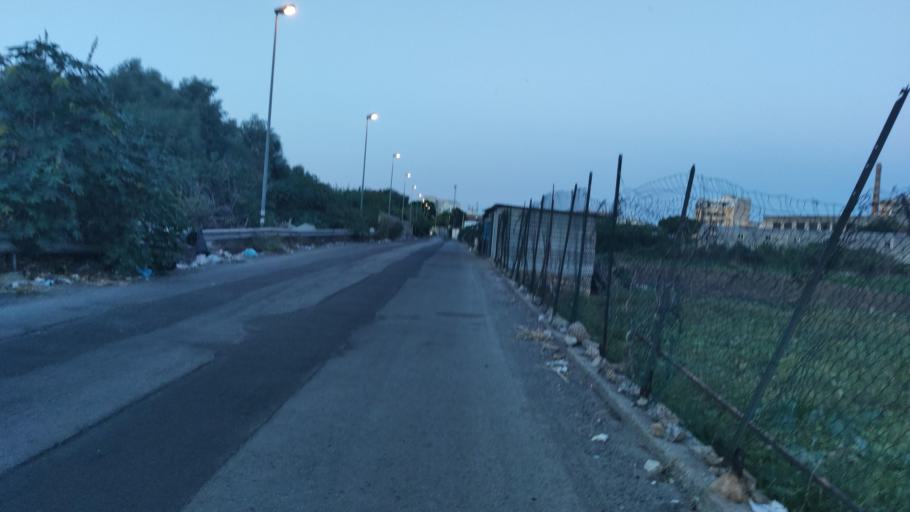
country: IT
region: Sicily
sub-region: Palermo
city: Ciaculli
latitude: 38.1025
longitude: 13.3709
